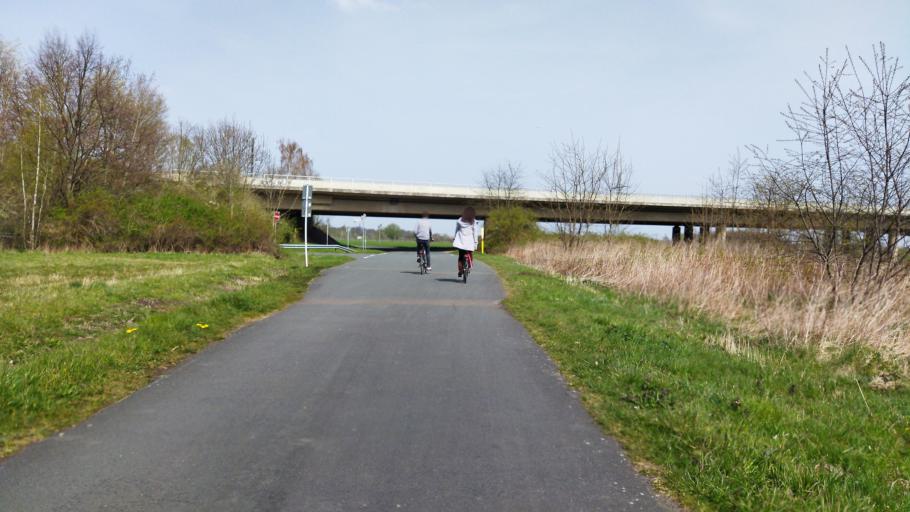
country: DE
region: North Rhine-Westphalia
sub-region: Regierungsbezirk Detmold
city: Minden
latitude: 52.2692
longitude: 8.9250
